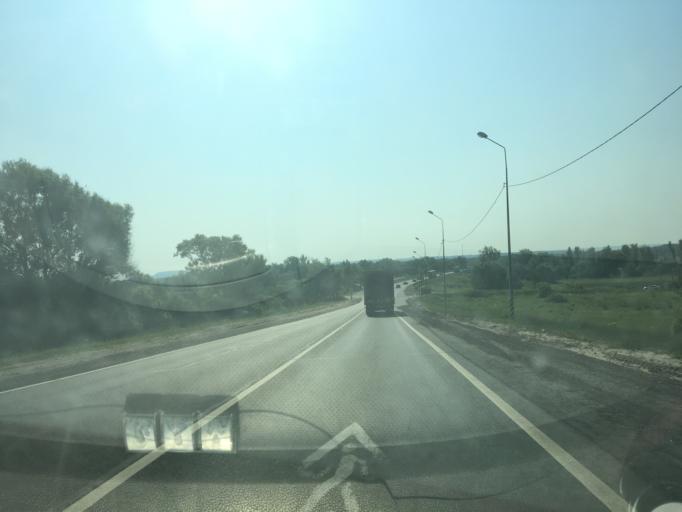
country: RU
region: Nizjnij Novgorod
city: Kstovo
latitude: 56.1008
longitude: 44.3035
